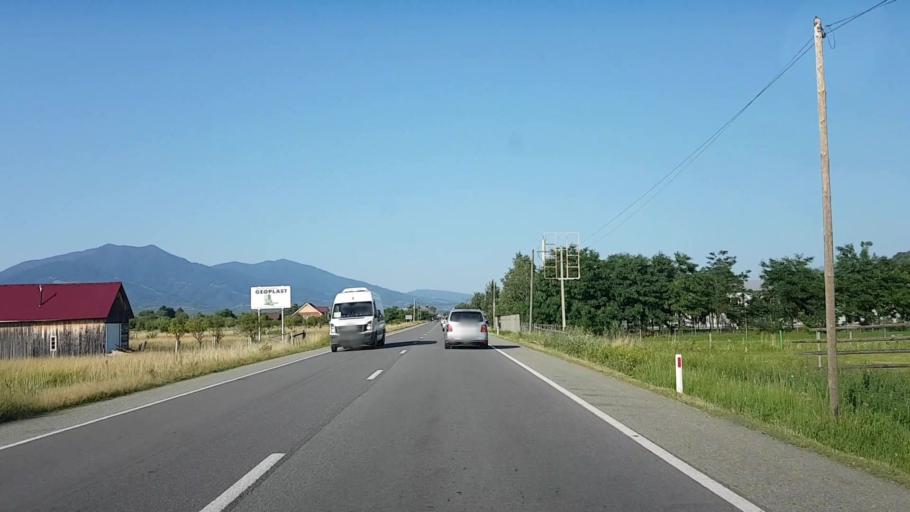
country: RO
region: Bistrita-Nasaud
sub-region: Comuna Livezile
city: Livezile
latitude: 47.1961
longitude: 24.6240
